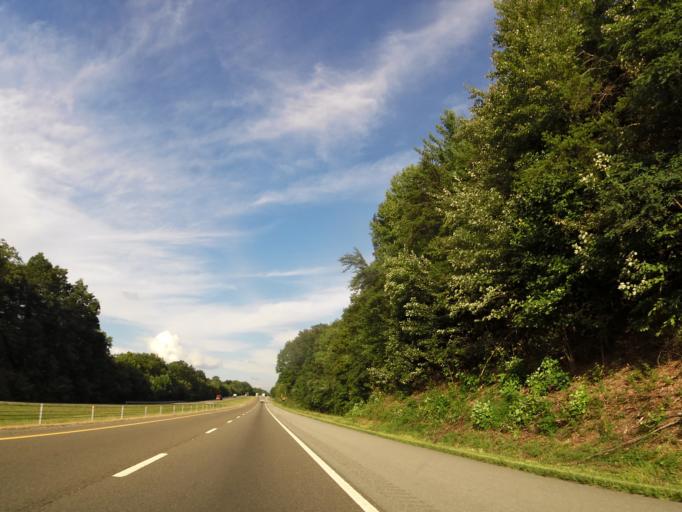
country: US
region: Tennessee
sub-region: Campbell County
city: Hunter
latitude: 36.4654
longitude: -84.2450
